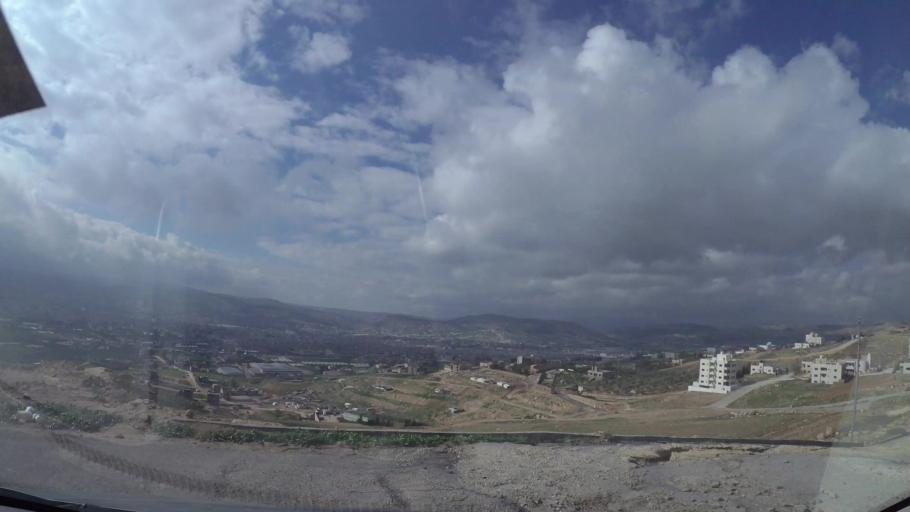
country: JO
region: Amman
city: Al Jubayhah
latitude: 32.0588
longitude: 35.8610
